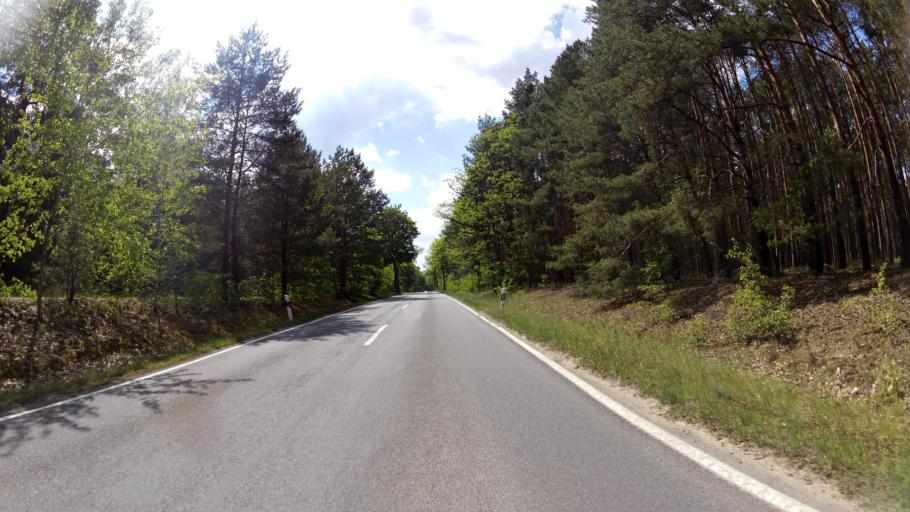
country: DE
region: Brandenburg
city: Gross Koris
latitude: 52.1660
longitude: 13.6808
